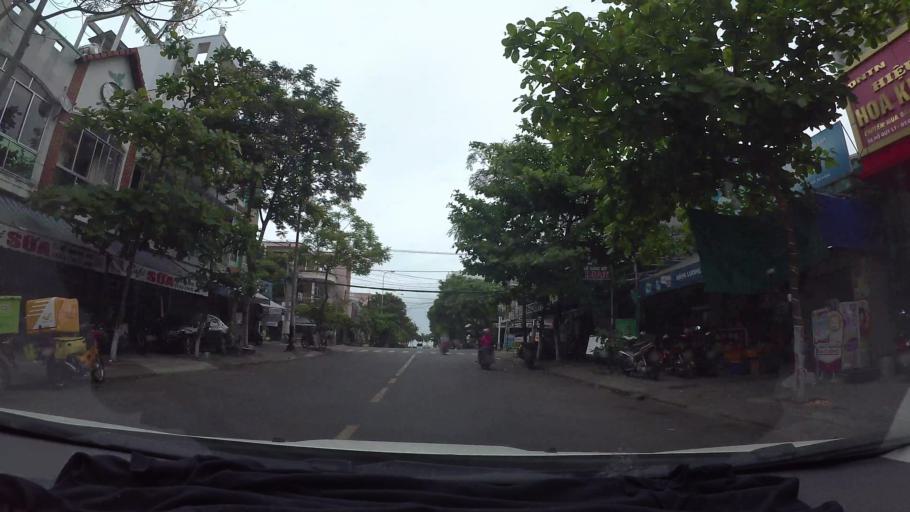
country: VN
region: Da Nang
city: Lien Chieu
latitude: 16.0761
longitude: 108.1724
